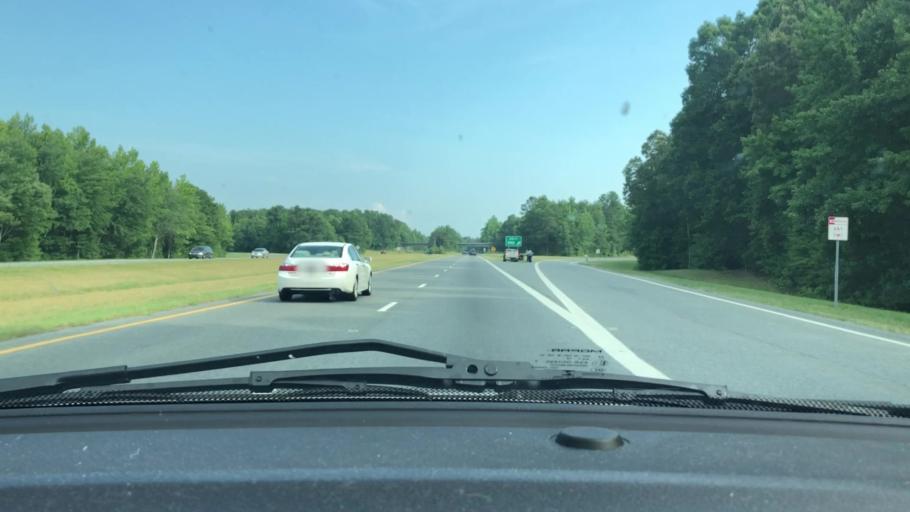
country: US
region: North Carolina
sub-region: Guilford County
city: Forest Oaks
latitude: 35.9198
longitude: -79.6776
